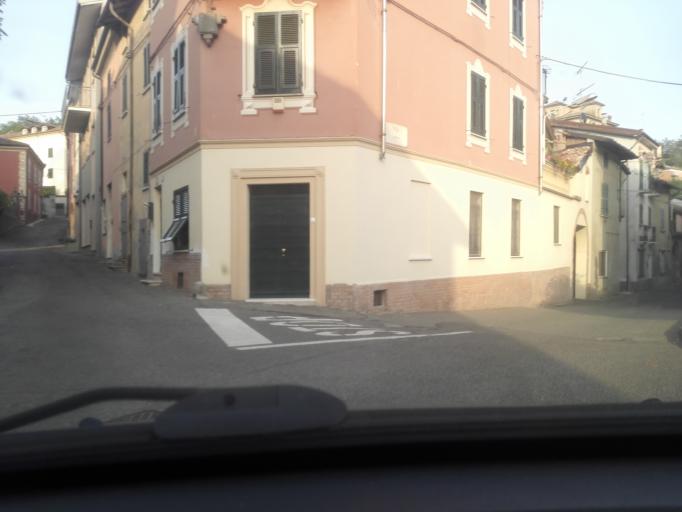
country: IT
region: Piedmont
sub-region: Provincia di Alessandria
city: Villalvernia
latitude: 44.8166
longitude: 8.8566
